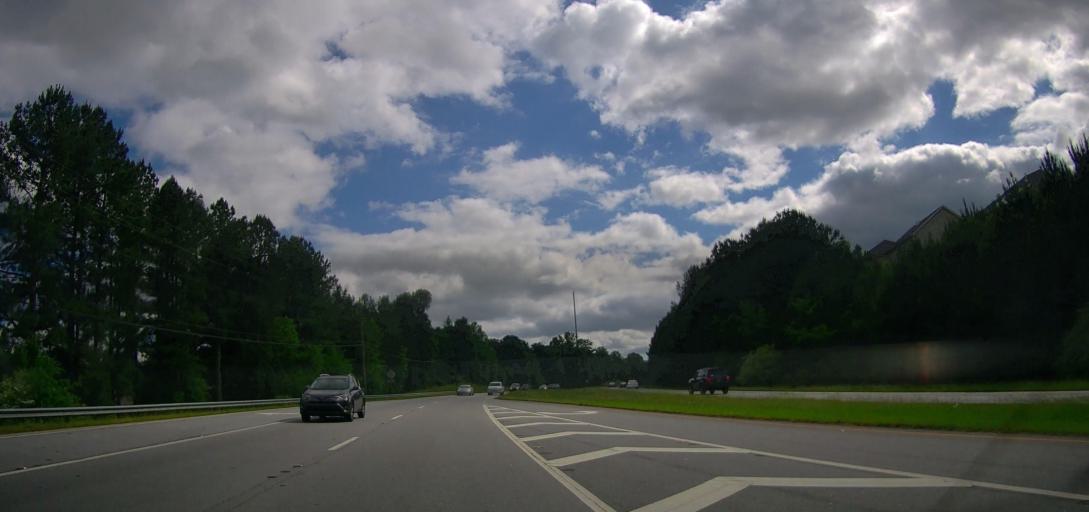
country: US
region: Georgia
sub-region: Rockdale County
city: Conyers
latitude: 33.6839
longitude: -83.9626
